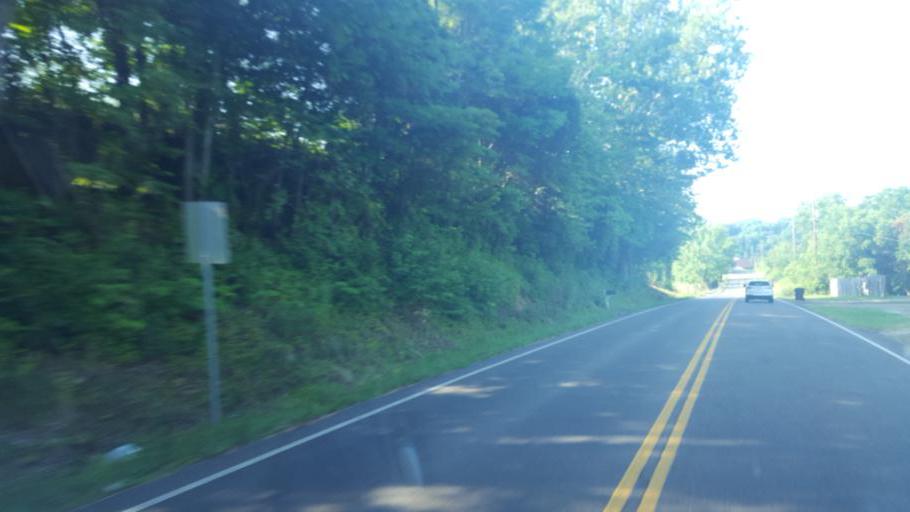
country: US
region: Tennessee
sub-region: Sullivan County
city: Bluff City
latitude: 36.4908
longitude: -82.2627
